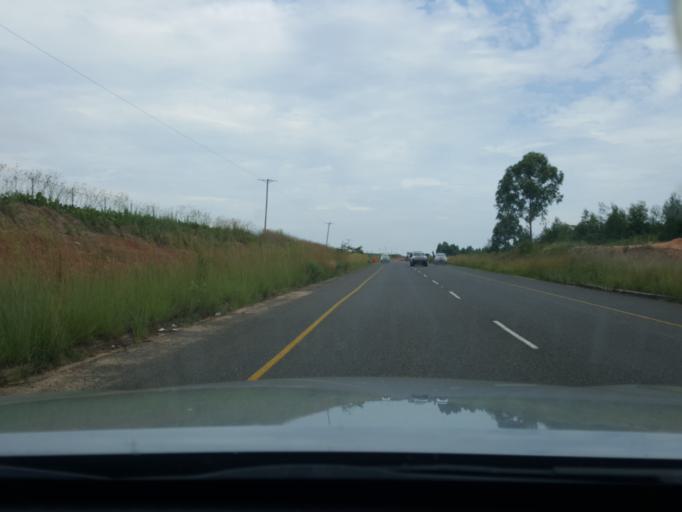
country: ZA
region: Mpumalanga
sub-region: Ehlanzeni District
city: White River
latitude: -25.2986
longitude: 30.9808
